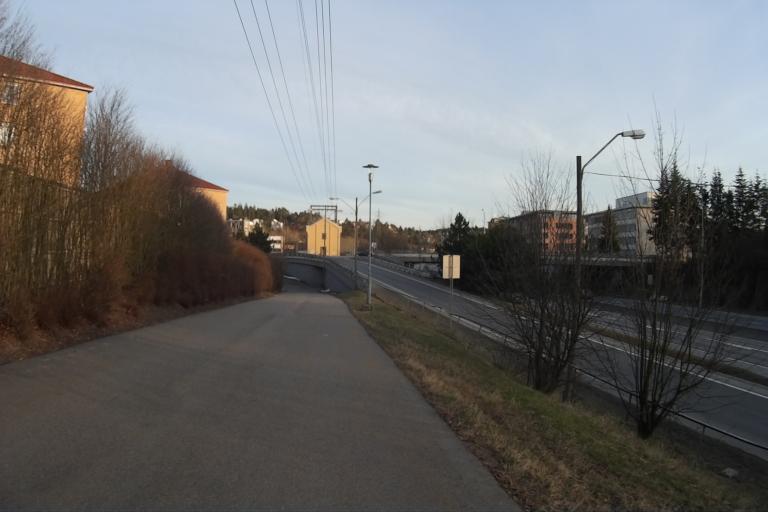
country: NO
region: Oslo
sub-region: Oslo
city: Oslo
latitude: 59.9135
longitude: 10.8165
